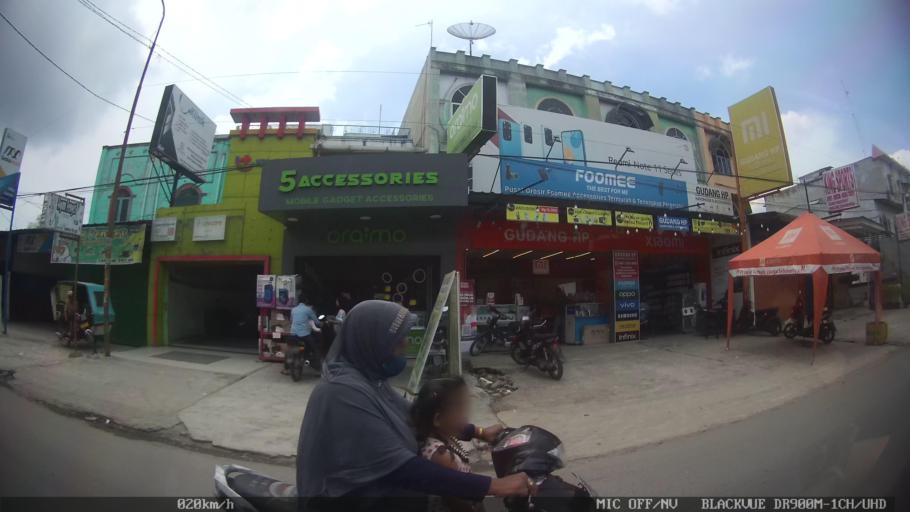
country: ID
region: North Sumatra
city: Labuhan Deli
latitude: 3.7017
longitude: 98.6579
